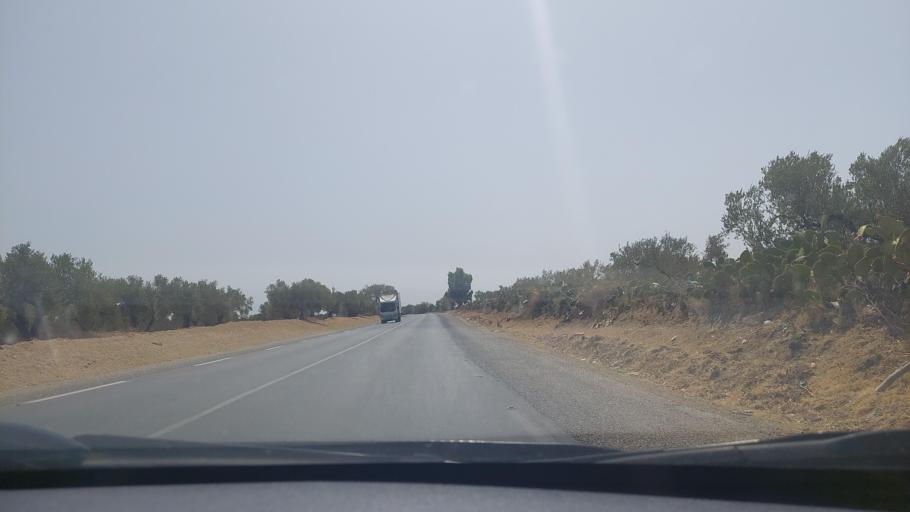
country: TN
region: Al Munastir
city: Sidi Bin Nur
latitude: 35.5728
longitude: 10.9104
